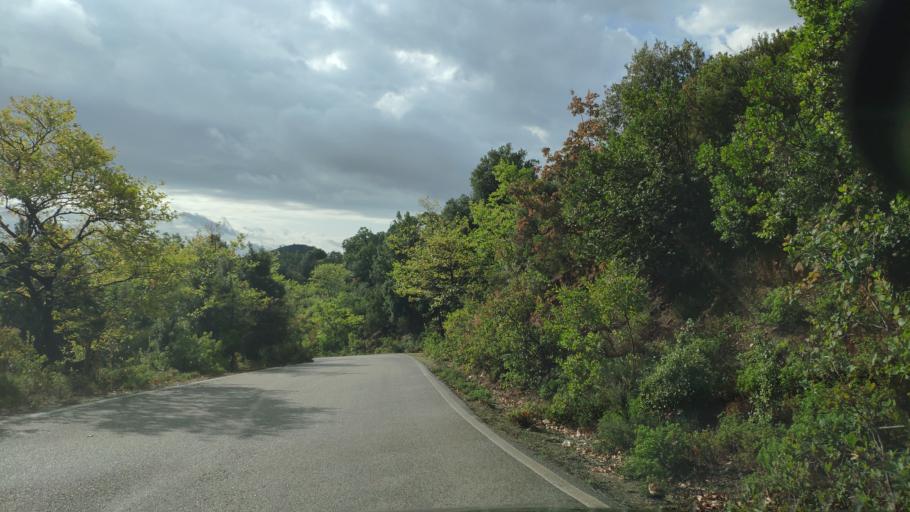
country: GR
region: West Greece
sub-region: Nomos Aitolias kai Akarnanias
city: Sardinia
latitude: 38.8605
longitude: 21.3041
